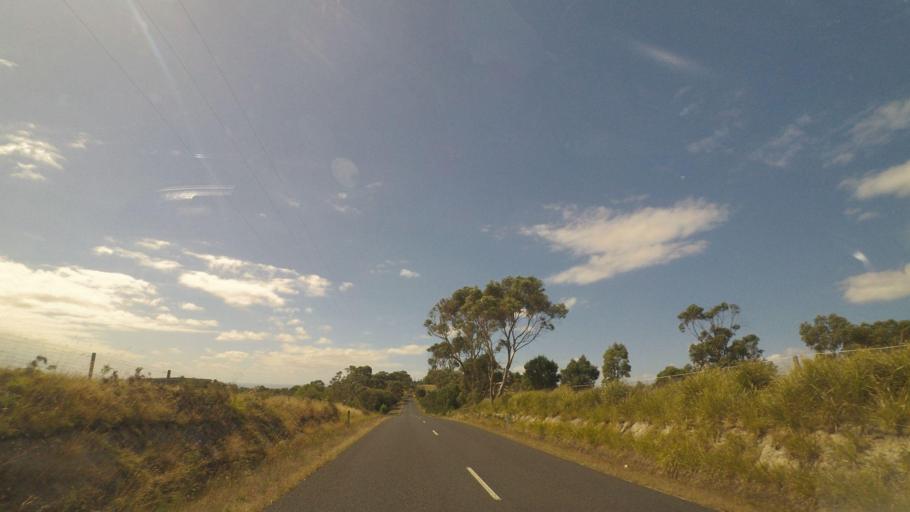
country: AU
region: Victoria
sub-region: Cardinia
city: Koo-Wee-Rup
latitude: -38.2993
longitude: 145.6692
